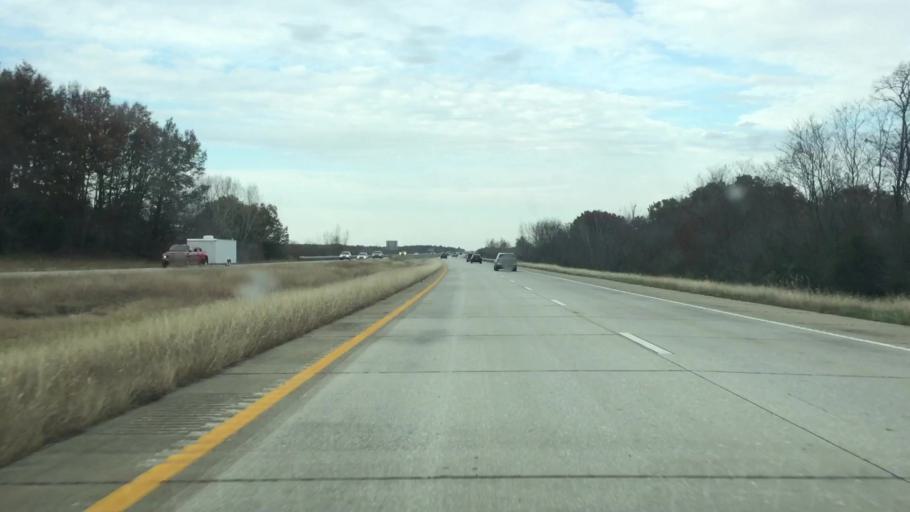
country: US
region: Missouri
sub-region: Henry County
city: Clinton
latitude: 38.2655
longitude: -93.7601
